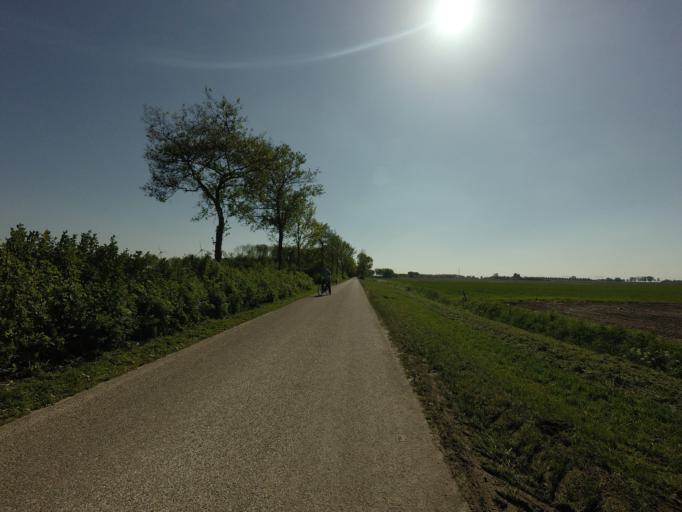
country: NL
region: North Brabant
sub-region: Gemeente Moerdijk
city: Klundert
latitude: 51.6328
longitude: 4.6079
